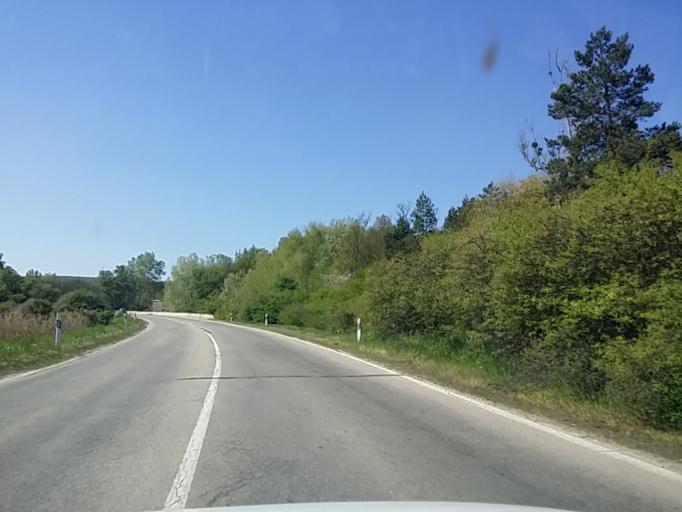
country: HU
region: Pest
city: Domony
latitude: 47.6258
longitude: 19.4149
